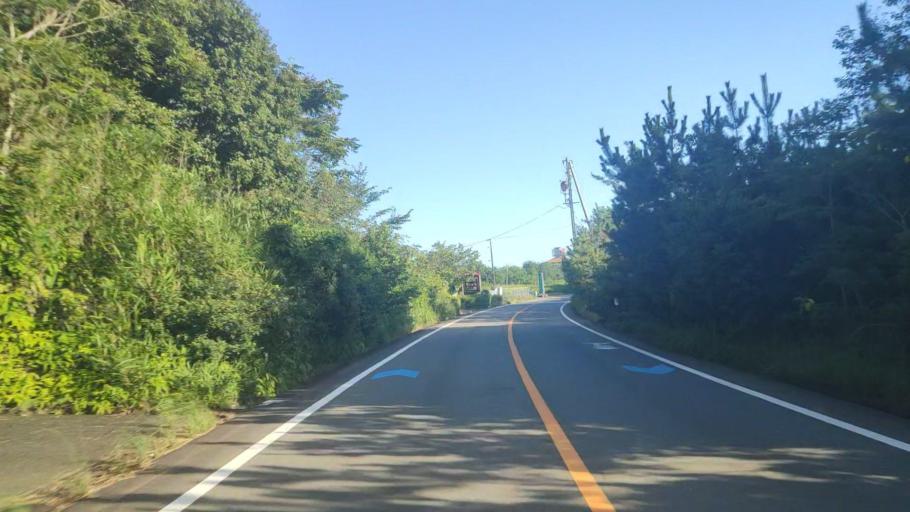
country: JP
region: Mie
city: Toba
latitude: 34.3412
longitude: 136.8401
